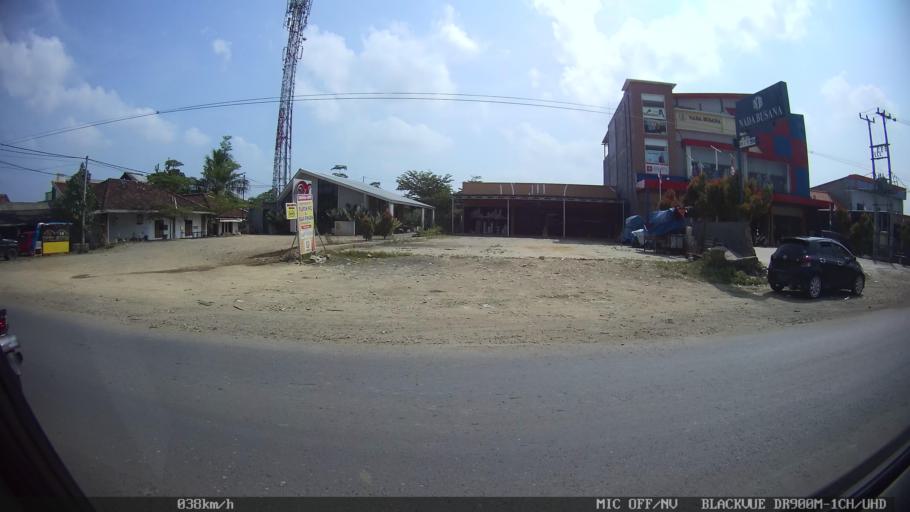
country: ID
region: Lampung
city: Pringsewu
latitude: -5.3628
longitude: 104.9996
